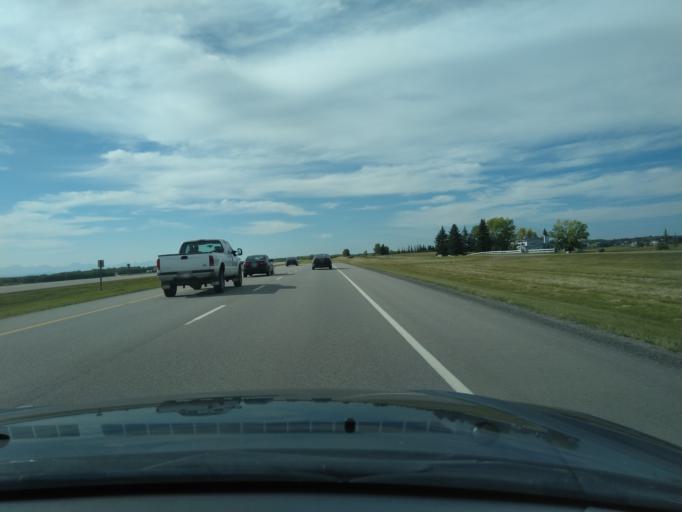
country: CA
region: Alberta
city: Cochrane
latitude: 51.1624
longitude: -114.2900
